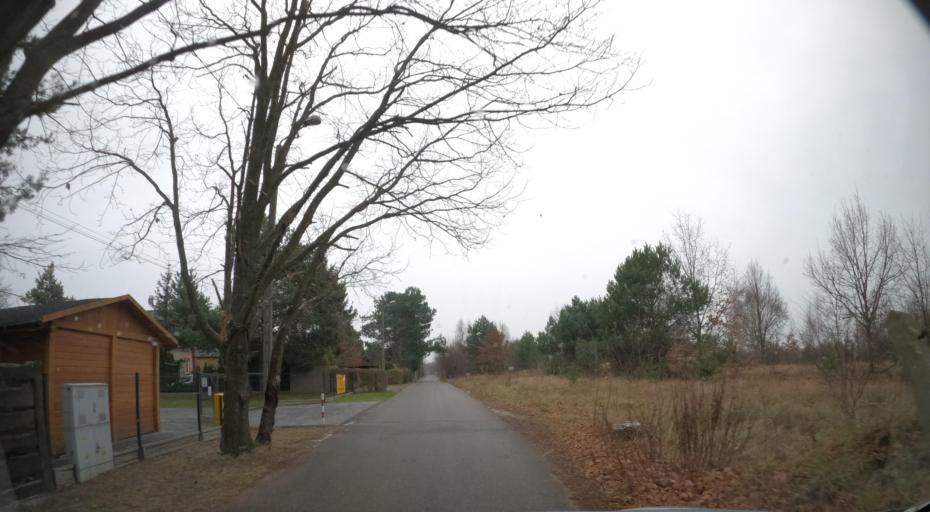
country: PL
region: Masovian Voivodeship
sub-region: Powiat radomski
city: Jastrzebia
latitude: 51.4326
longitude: 21.2290
